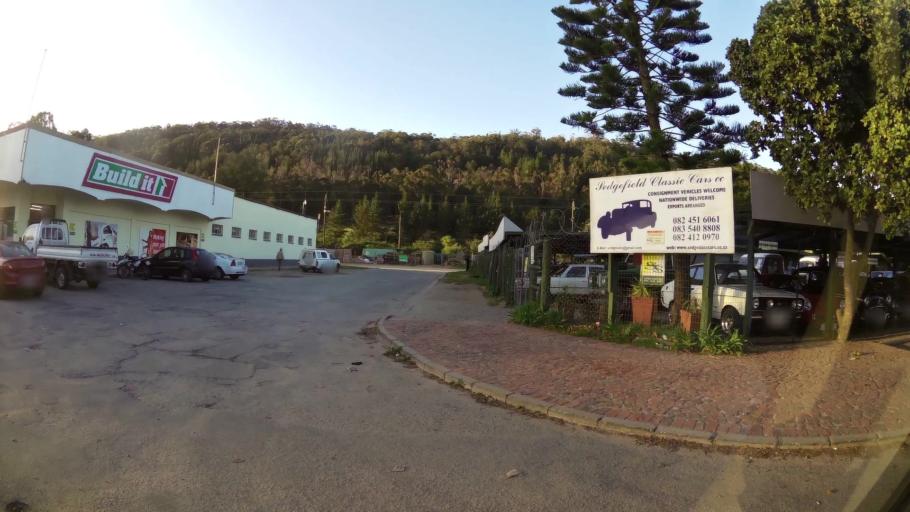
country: ZA
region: Western Cape
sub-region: Eden District Municipality
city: Knysna
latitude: -34.0146
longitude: 22.8039
